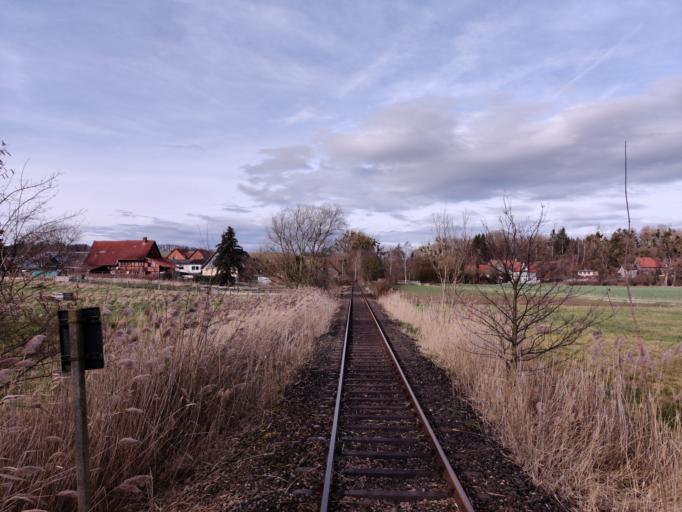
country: DE
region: Lower Saxony
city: Bockenem
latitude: 51.9818
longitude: 10.1196
